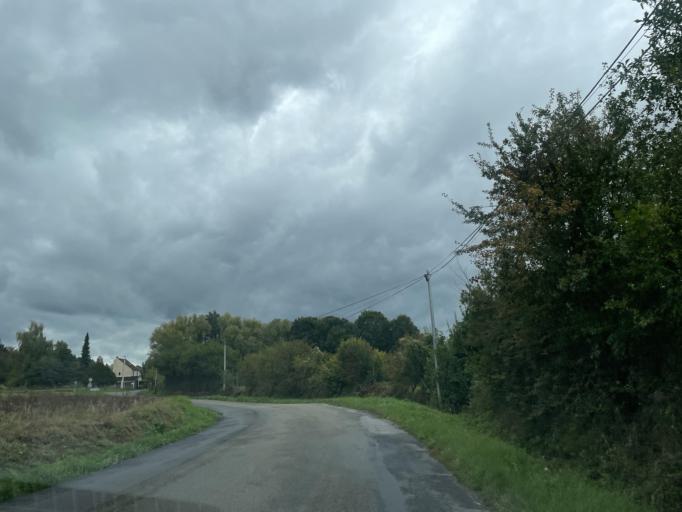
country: FR
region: Ile-de-France
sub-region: Departement de Seine-et-Marne
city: Chailly-en-Brie
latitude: 48.8091
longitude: 3.1156
